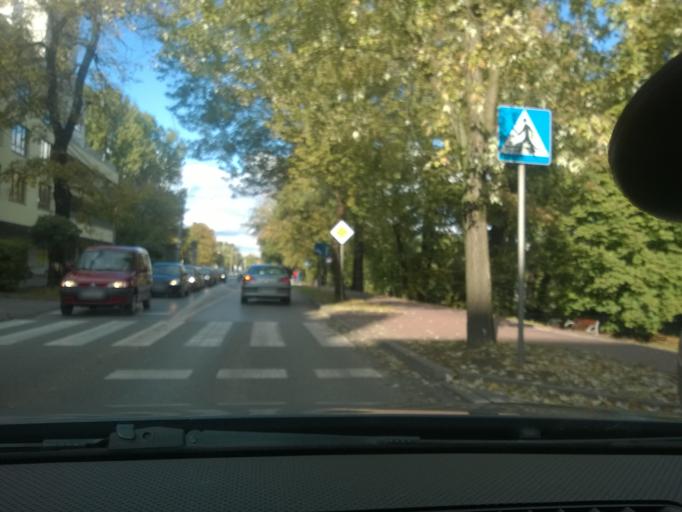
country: PL
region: Masovian Voivodeship
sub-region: Powiat pruszkowski
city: Pruszkow
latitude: 52.1669
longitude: 20.8090
